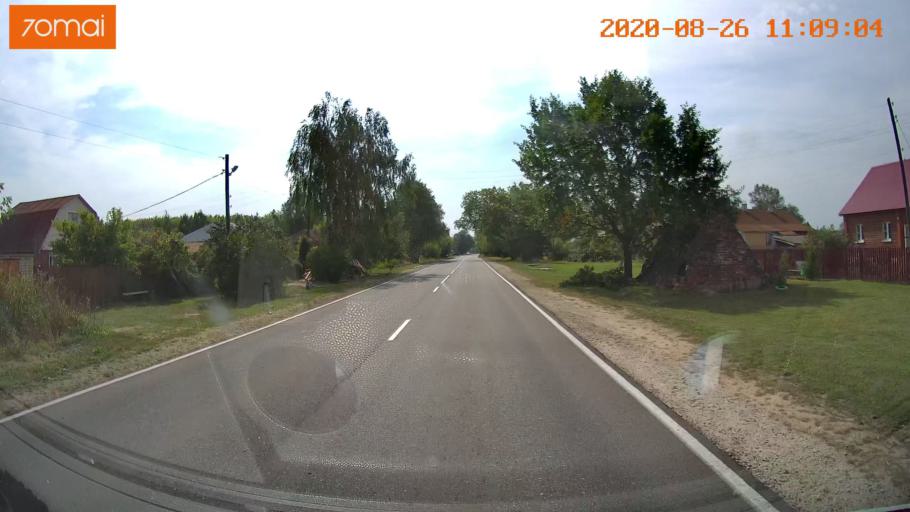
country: RU
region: Rjazan
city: Izhevskoye
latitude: 54.4955
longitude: 41.1232
